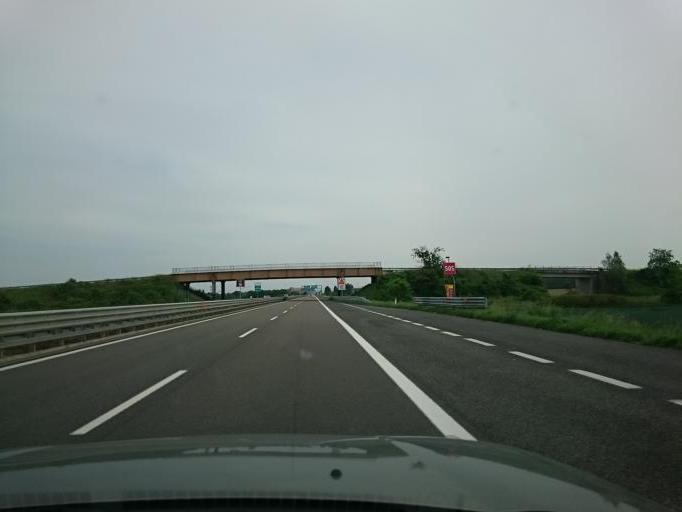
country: IT
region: Veneto
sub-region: Provincia di Venezia
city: Tessera
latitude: 45.5196
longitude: 12.3320
